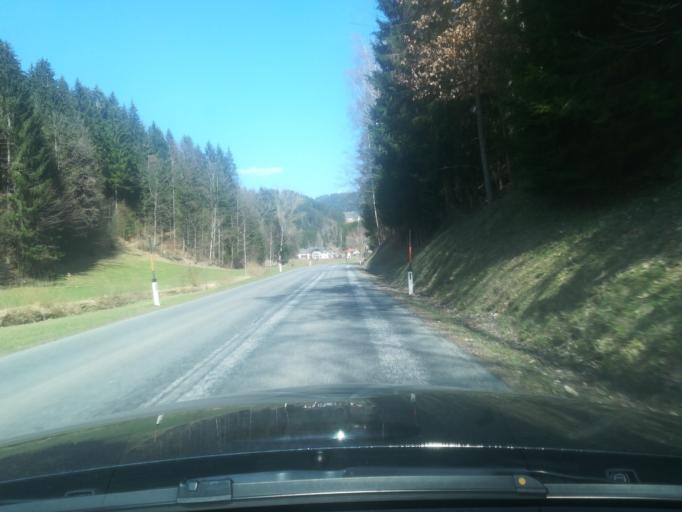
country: AT
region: Upper Austria
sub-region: Politischer Bezirk Perg
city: Sankt Georgen am Walde
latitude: 48.4418
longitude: 14.7822
